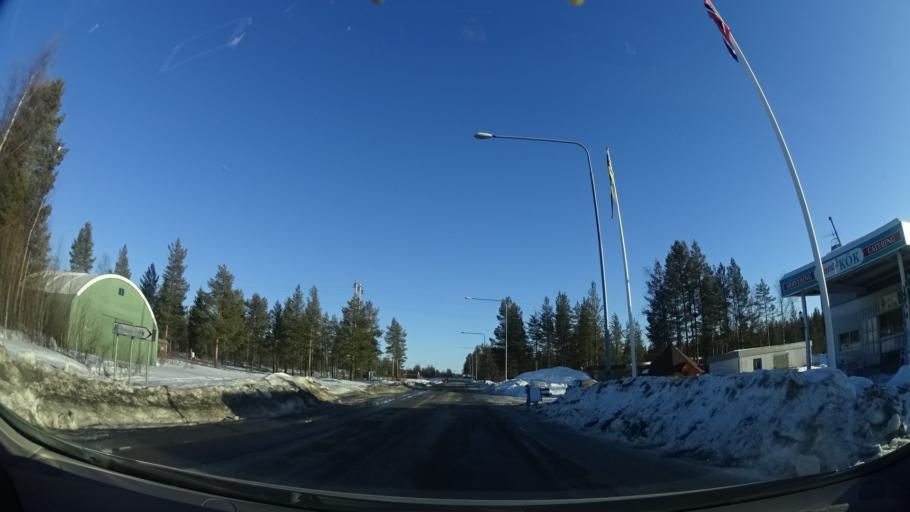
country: SE
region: Vaesterbotten
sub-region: Skelleftea Kommun
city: Langsele
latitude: 65.0546
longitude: 20.0535
